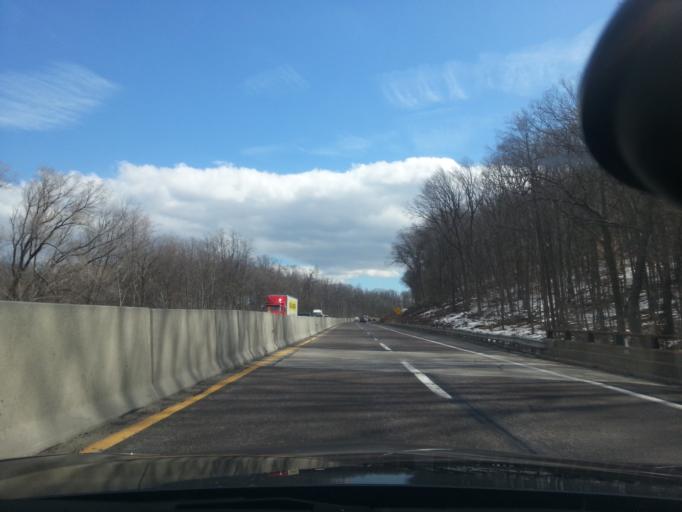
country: US
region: Pennsylvania
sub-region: Lehigh County
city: Emmaus
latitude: 40.5157
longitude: -75.5066
